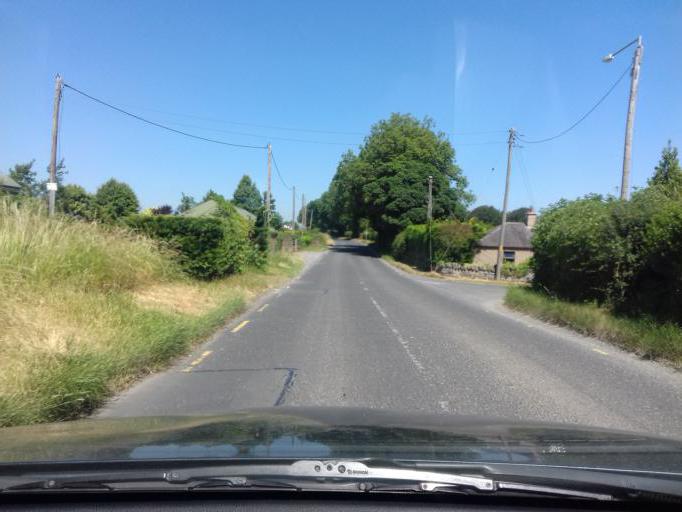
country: IE
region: Leinster
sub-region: Fingal County
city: Swords
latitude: 53.4927
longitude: -6.2692
